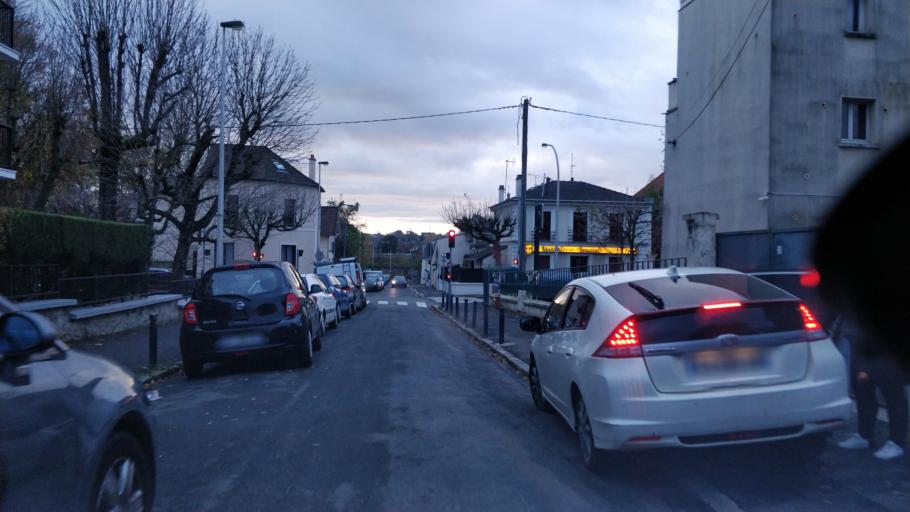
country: FR
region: Ile-de-France
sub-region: Departement de Seine-Saint-Denis
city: Le Raincy
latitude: 48.8888
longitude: 2.5191
